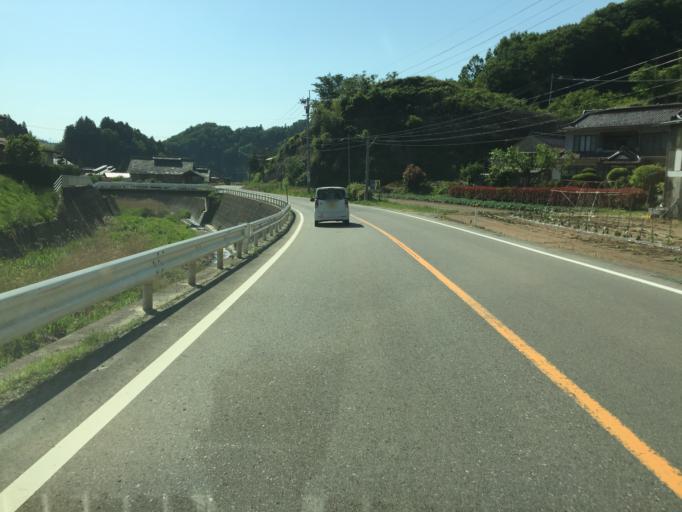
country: JP
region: Fukushima
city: Yanagawamachi-saiwaicho
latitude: 37.7595
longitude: 140.6443
